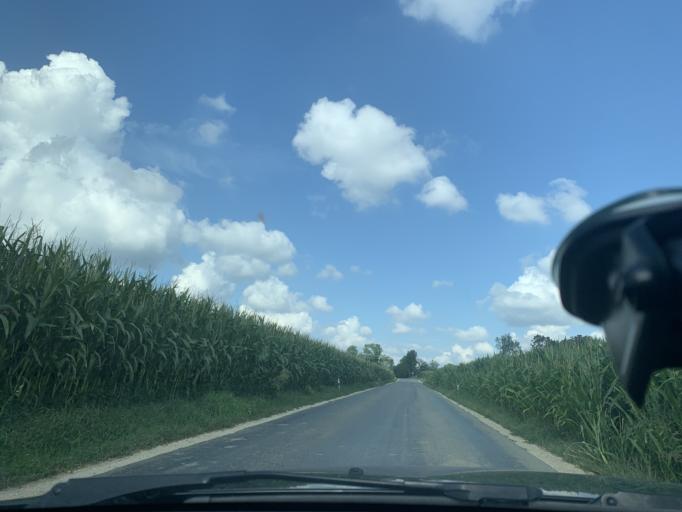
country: DE
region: Bavaria
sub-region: Swabia
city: Kissing
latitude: 48.2929
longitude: 10.9946
